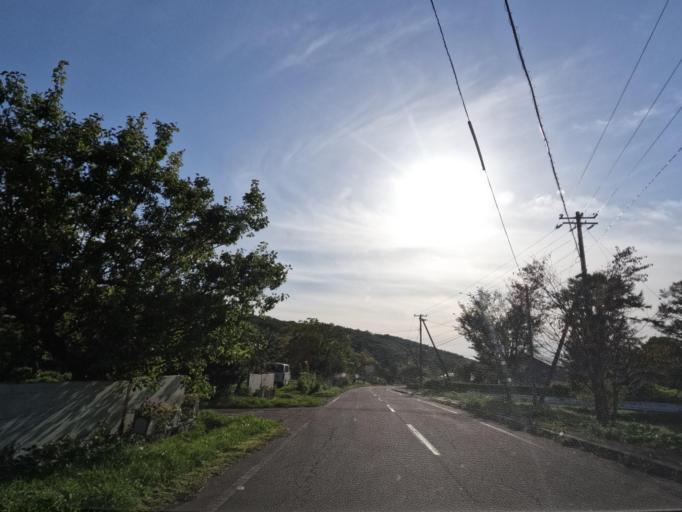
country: JP
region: Hokkaido
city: Date
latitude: 42.3991
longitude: 140.9233
